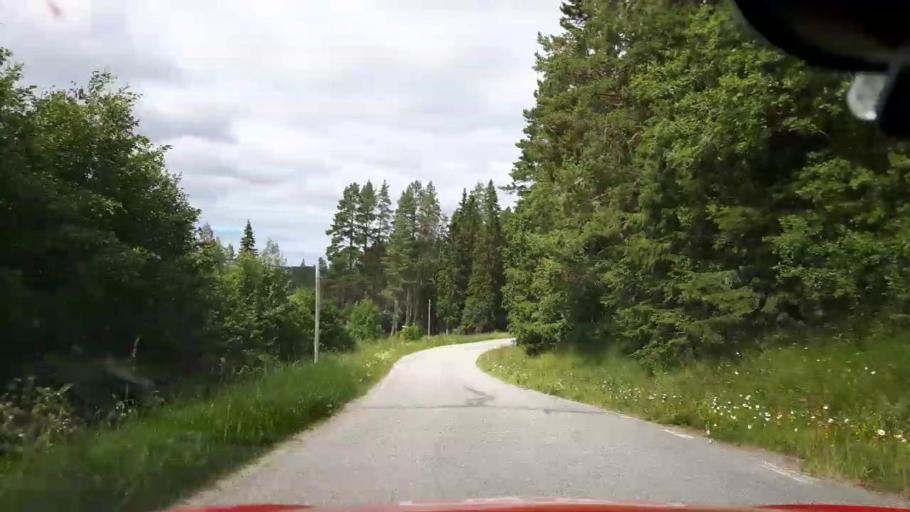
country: SE
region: Jaemtland
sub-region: Braecke Kommun
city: Braecke
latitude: 62.8617
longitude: 15.2759
